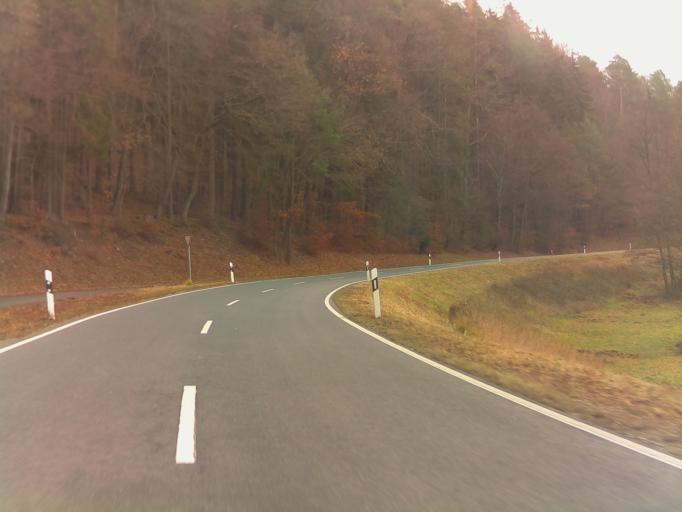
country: DE
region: Bavaria
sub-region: Regierungsbezirk Unterfranken
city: Monchberg
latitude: 49.8134
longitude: 9.3023
